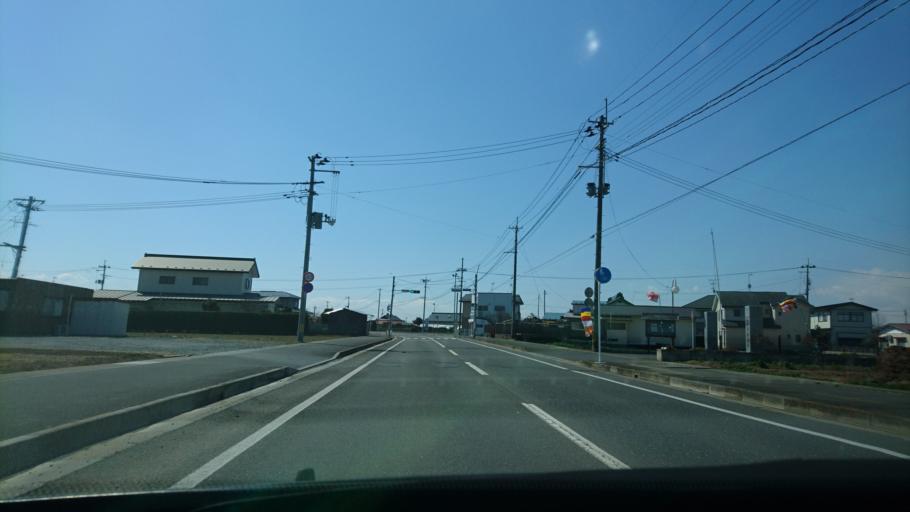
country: JP
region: Iwate
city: Ichinoseki
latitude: 38.7684
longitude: 141.1398
